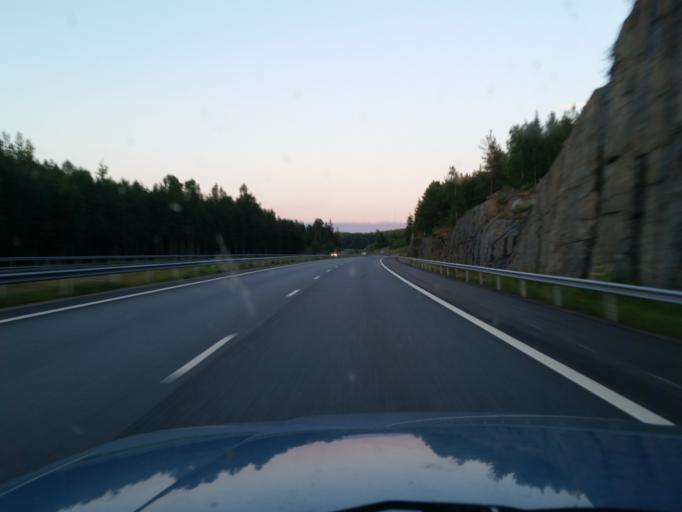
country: FI
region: Uusimaa
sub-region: Helsinki
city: Sammatti
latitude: 60.3809
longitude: 23.7827
